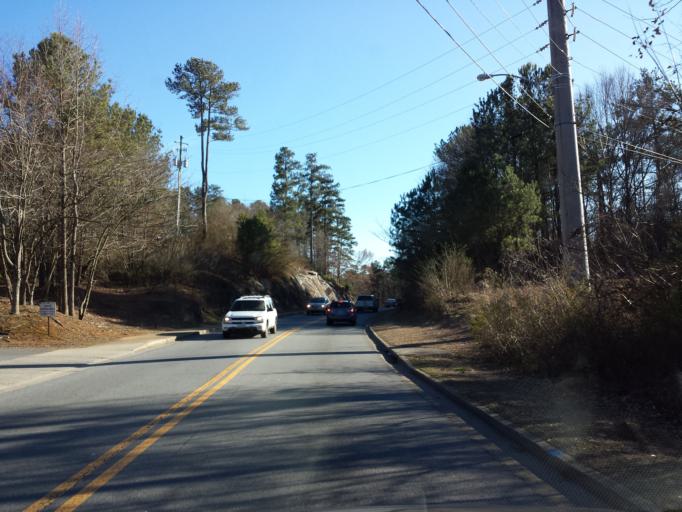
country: US
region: Georgia
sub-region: Cobb County
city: Marietta
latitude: 33.9686
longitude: -84.5147
